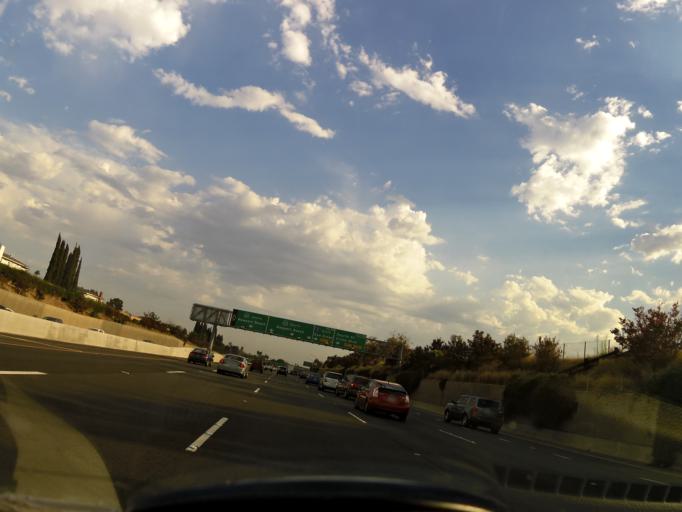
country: US
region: California
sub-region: Orange County
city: Tustin
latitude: 33.7552
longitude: -117.8316
